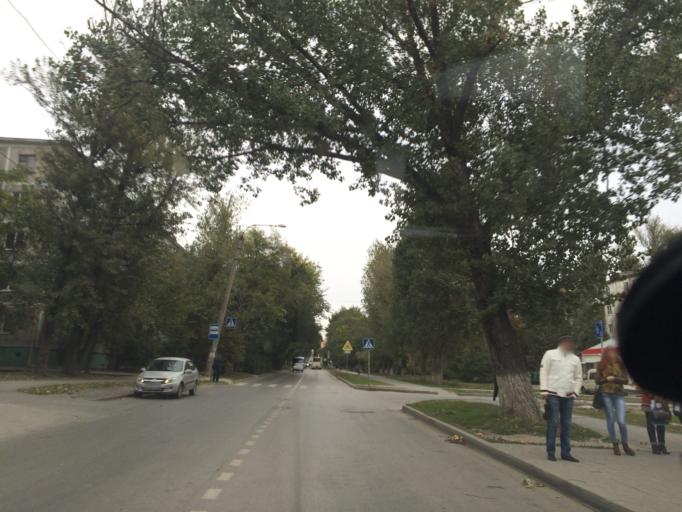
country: RU
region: Rostov
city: Rostov-na-Donu
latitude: 47.2034
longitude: 39.6156
